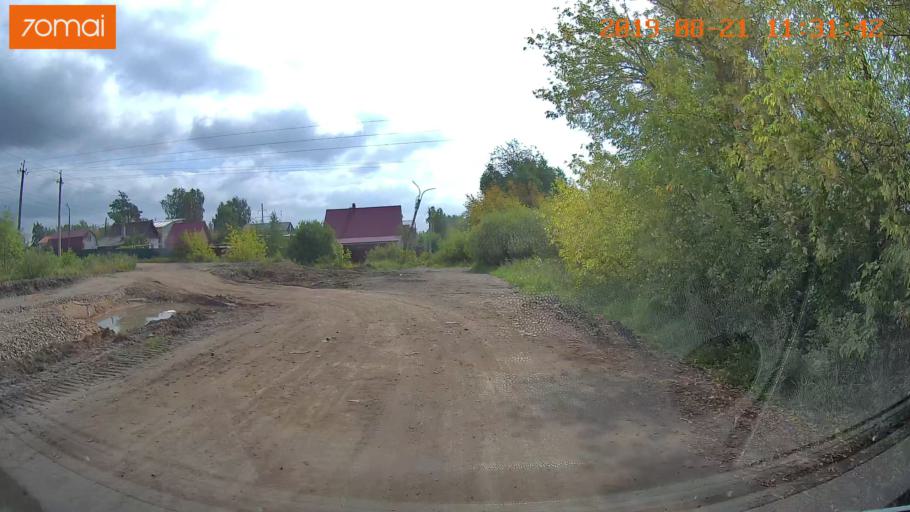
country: RU
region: Ivanovo
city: Novo-Talitsy
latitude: 56.9874
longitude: 40.9086
